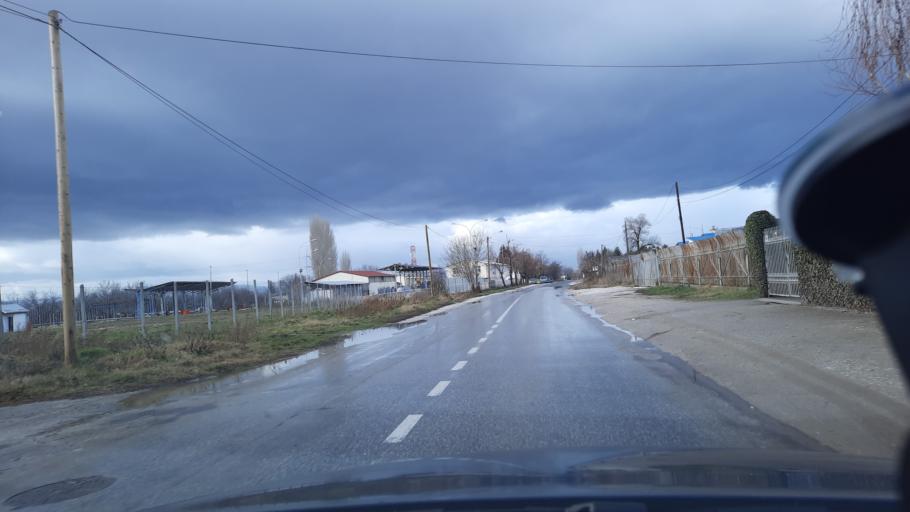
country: MK
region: Prilep
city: Markov Grad
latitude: 41.3432
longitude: 21.5262
